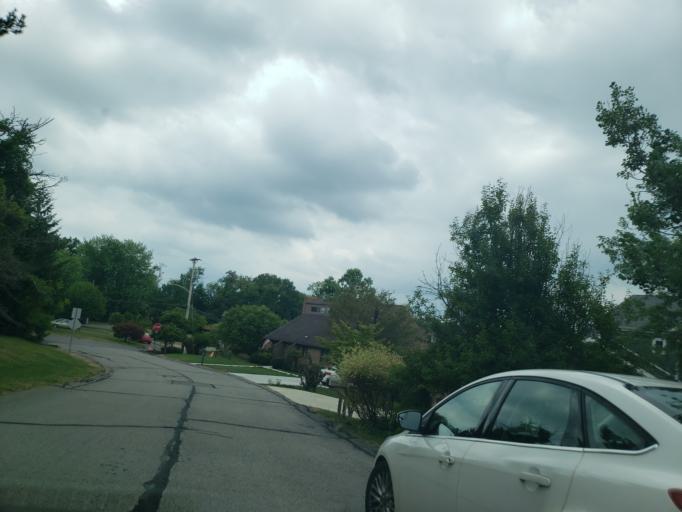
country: US
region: Pennsylvania
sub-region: Allegheny County
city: Coraopolis
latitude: 40.5321
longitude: -80.1613
